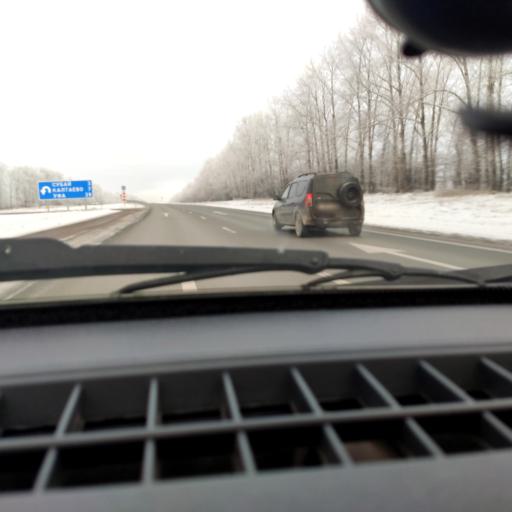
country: RU
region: Bashkortostan
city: Kushnarenkovo
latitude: 55.0296
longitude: 55.4642
